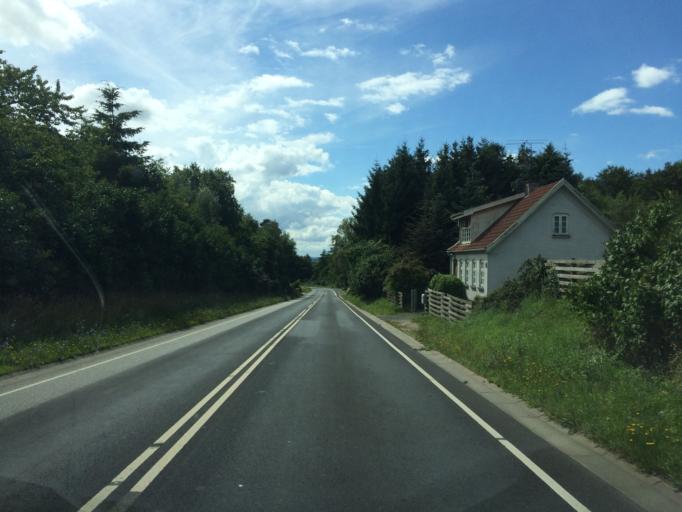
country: DK
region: South Denmark
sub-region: Faaborg-Midtfyn Kommune
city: Faaborg
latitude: 55.1242
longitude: 10.2521
